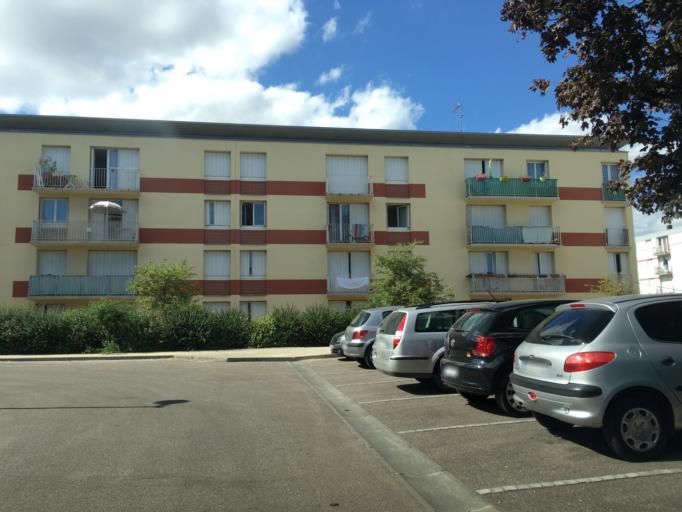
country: FR
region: Haute-Normandie
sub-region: Departement de l'Eure
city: Vernon
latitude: 49.0853
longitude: 1.4738
